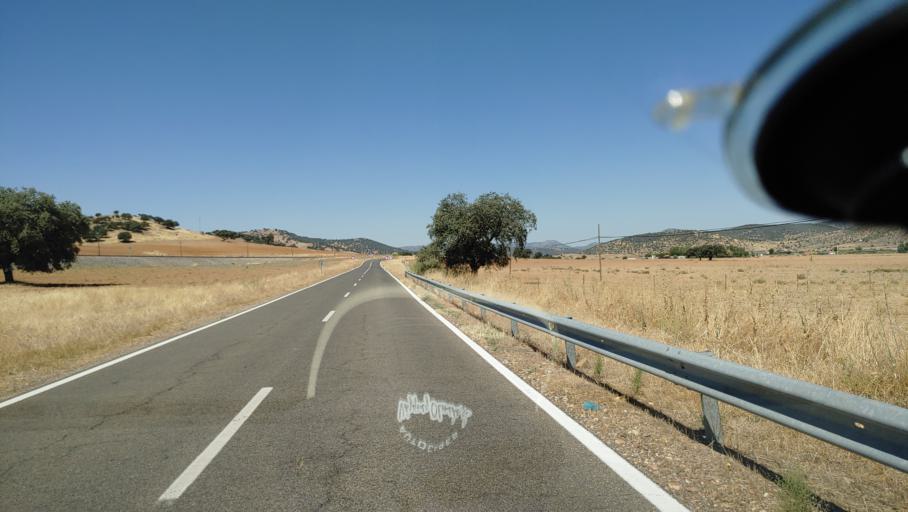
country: ES
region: Castille-La Mancha
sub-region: Provincia de Ciudad Real
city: Guadalmez
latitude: 38.7096
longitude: -4.9630
